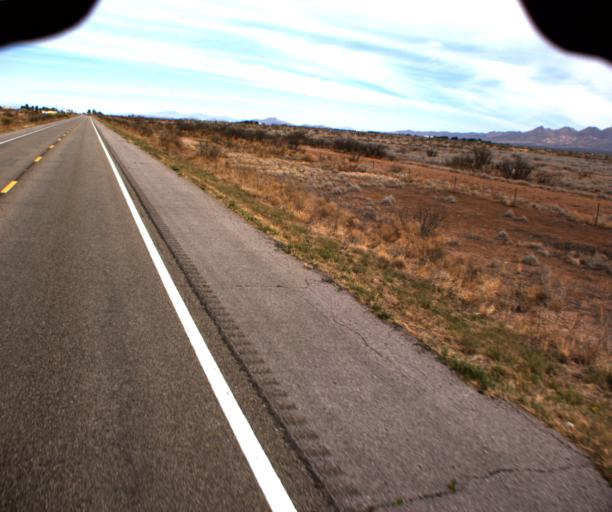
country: US
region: Arizona
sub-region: Cochise County
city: Pirtleville
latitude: 31.5815
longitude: -109.6687
